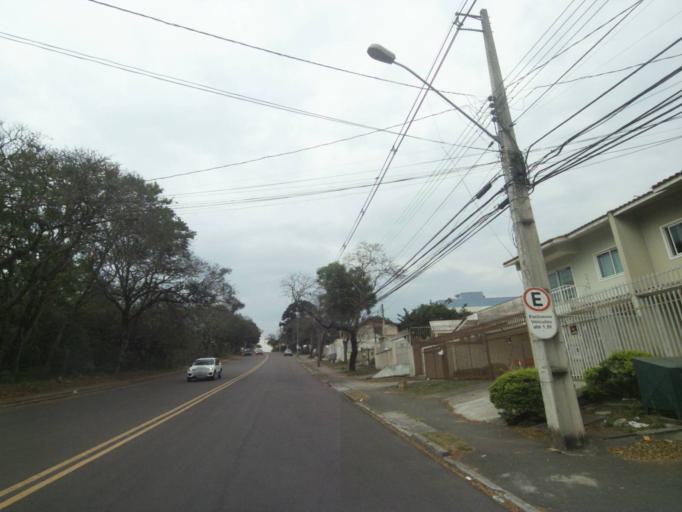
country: BR
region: Parana
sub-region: Pinhais
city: Pinhais
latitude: -25.4827
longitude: -49.2168
